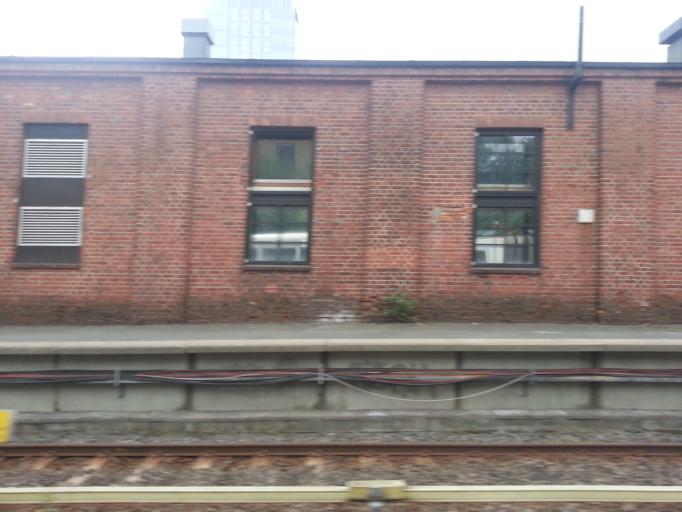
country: NO
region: Oslo
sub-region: Oslo
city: Sjolyststranda
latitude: 59.9310
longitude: 10.7135
